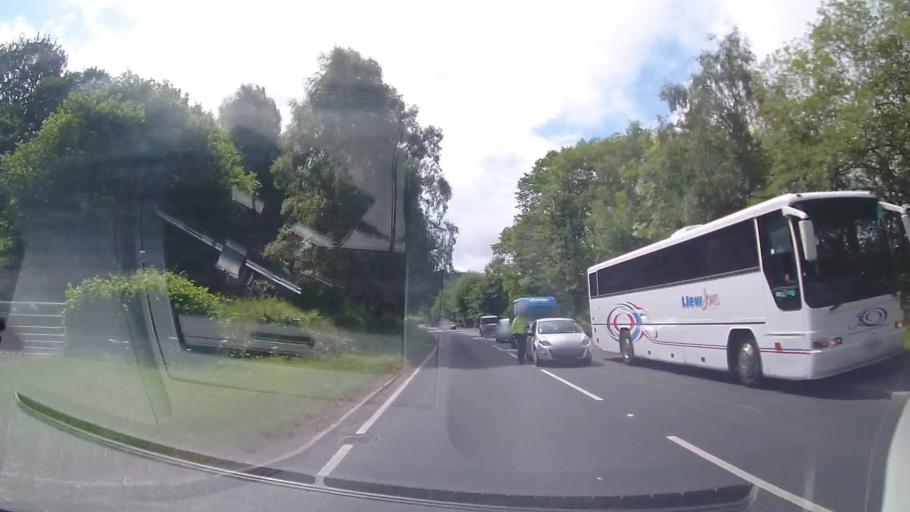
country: GB
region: Wales
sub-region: Denbighshire
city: Corwen
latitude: 52.9776
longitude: -3.3234
